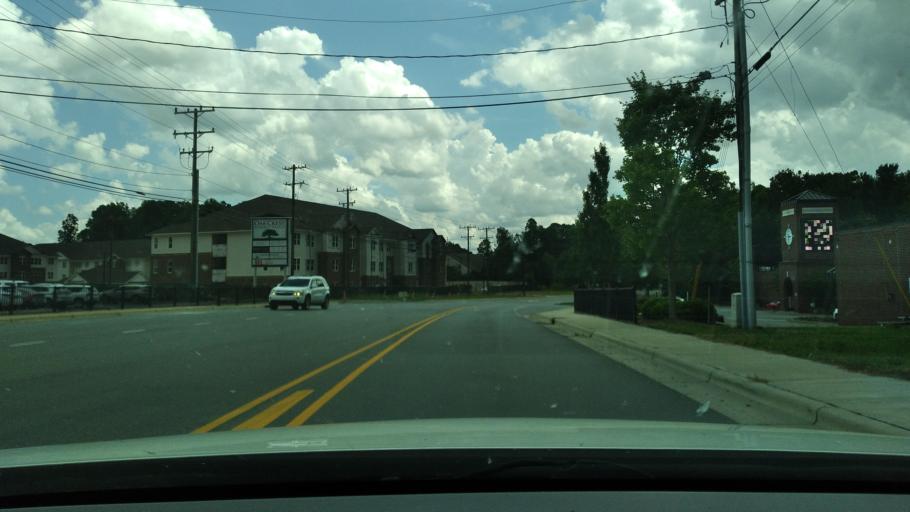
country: US
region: North Carolina
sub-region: Alamance County
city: Elon
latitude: 36.0793
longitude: -79.5138
